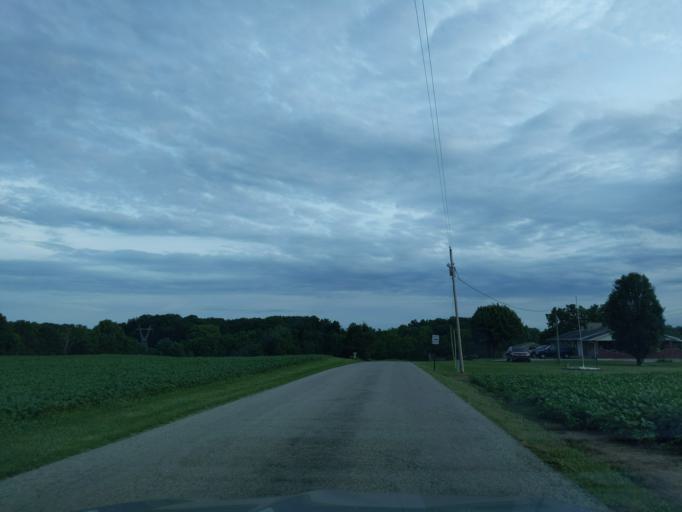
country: US
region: Indiana
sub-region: Ripley County
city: Sunman
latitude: 39.2924
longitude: -85.0908
